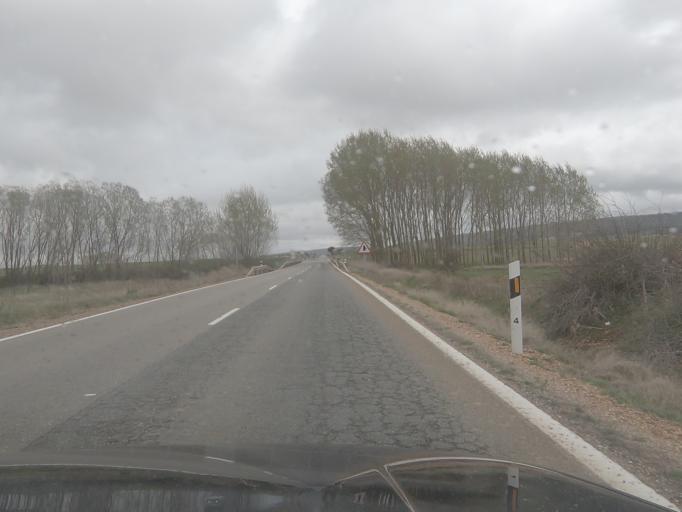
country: ES
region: Castille and Leon
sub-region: Provincia de Zamora
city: Pozuelo de Tabara
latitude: 41.7807
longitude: -5.8891
